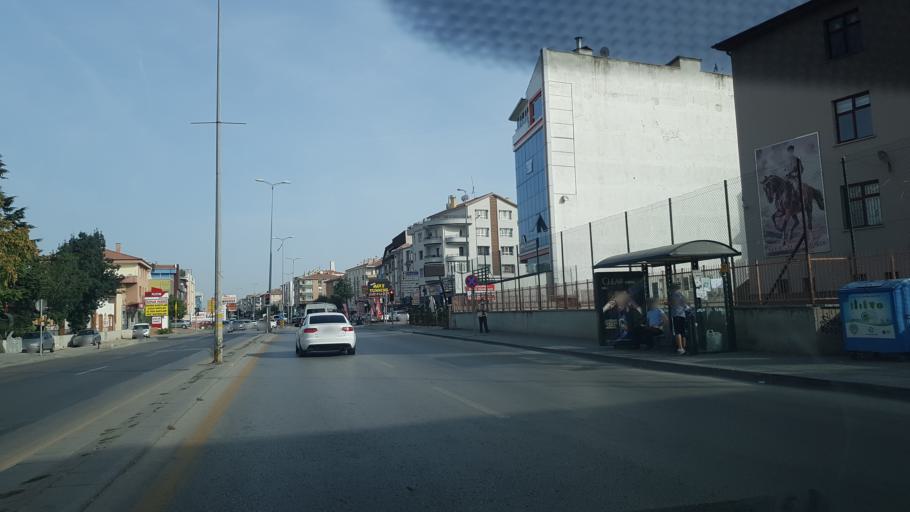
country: TR
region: Ankara
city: Etimesgut
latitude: 39.9514
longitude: 32.6482
